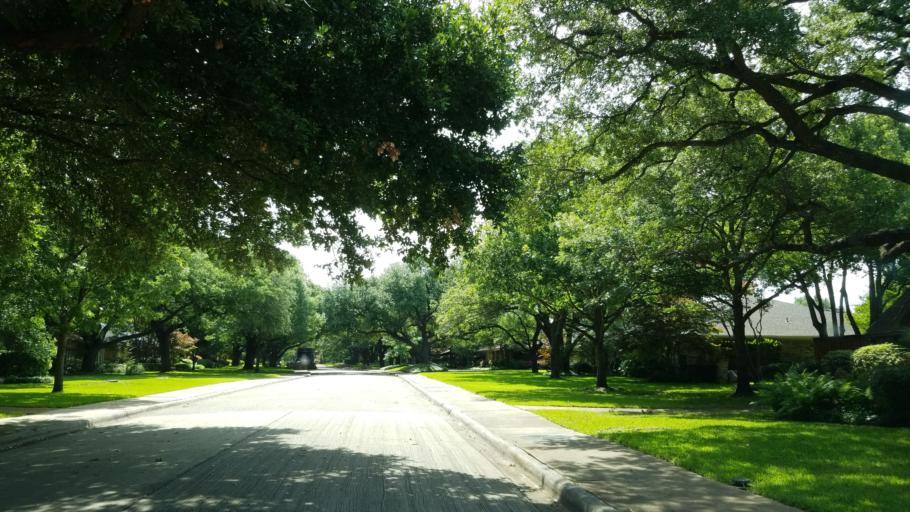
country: US
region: Texas
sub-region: Dallas County
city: Farmers Branch
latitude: 32.9052
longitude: -96.8470
